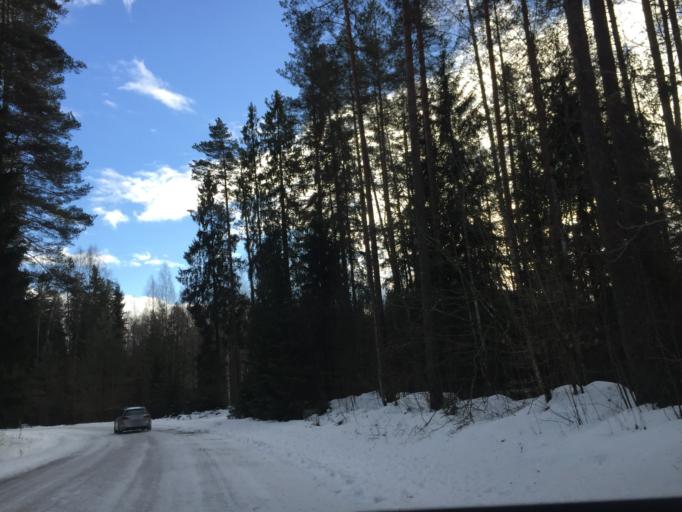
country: LV
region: Lielvarde
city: Lielvarde
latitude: 56.5626
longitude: 24.7988
